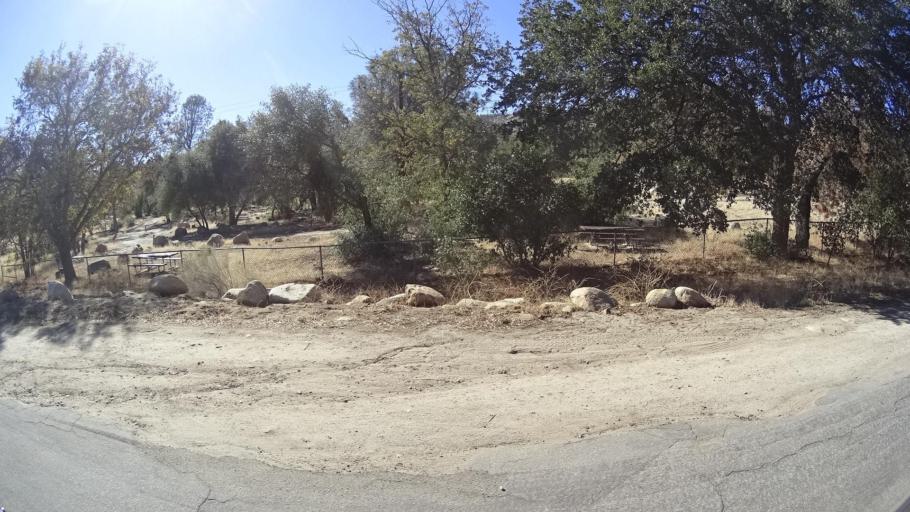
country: US
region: California
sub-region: Kern County
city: Wofford Heights
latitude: 35.7019
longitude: -118.4603
